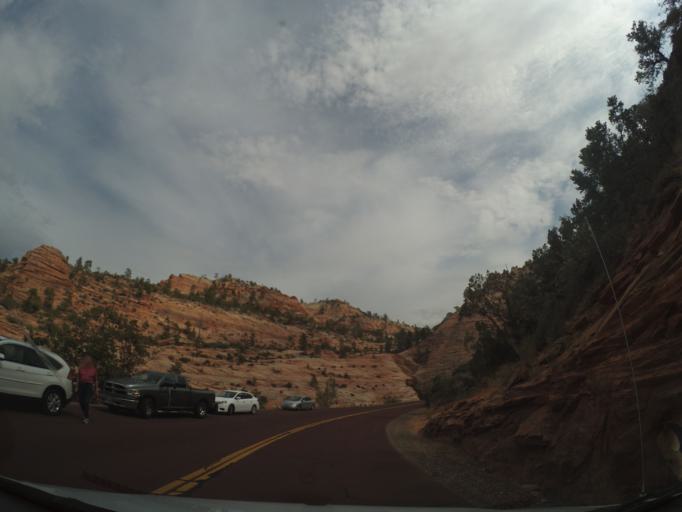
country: US
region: Utah
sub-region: Washington County
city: Hildale
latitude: 37.2176
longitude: -112.9182
